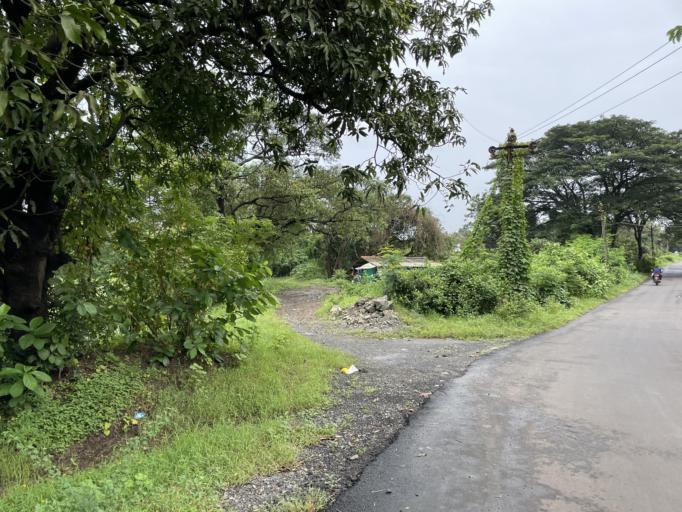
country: IN
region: Gujarat
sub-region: Valsad
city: Pardi
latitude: 20.4528
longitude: 72.9342
